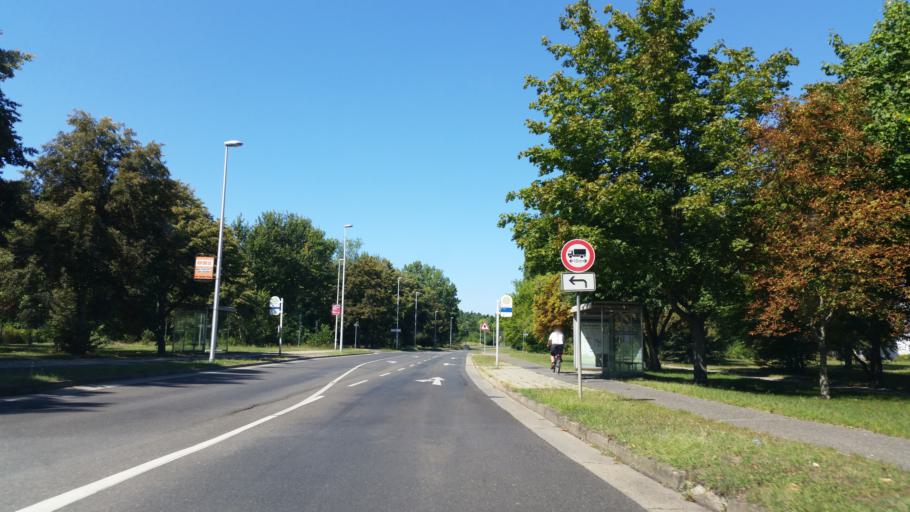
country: DE
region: Brandenburg
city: Cottbus
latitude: 51.7283
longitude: 14.3204
